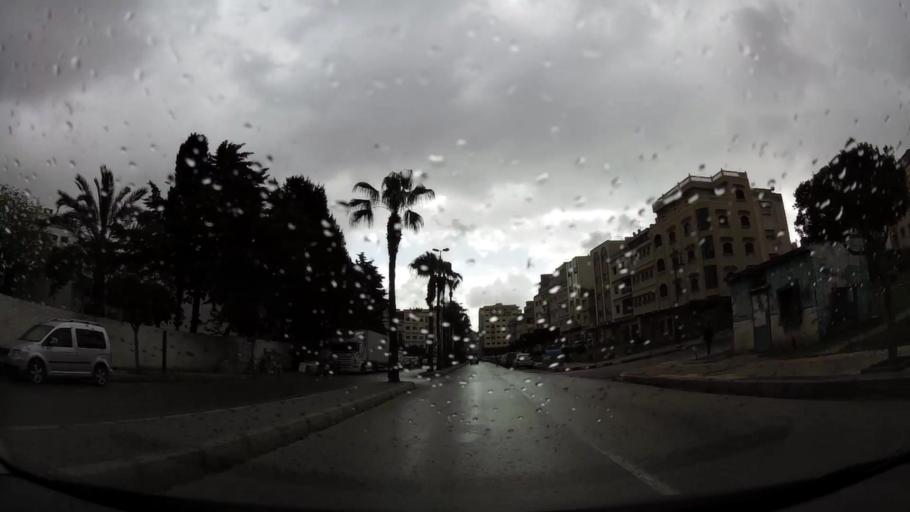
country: MA
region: Tanger-Tetouan
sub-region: Tanger-Assilah
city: Tangier
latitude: 35.7619
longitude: -5.8236
